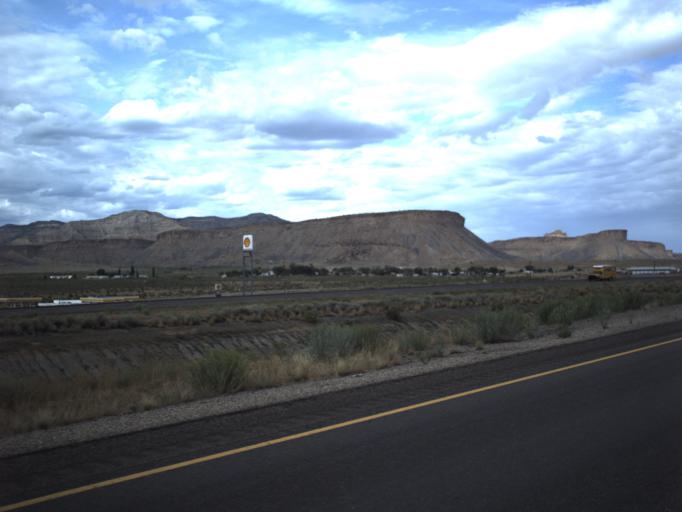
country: US
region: Utah
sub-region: Grand County
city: Moab
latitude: 38.9612
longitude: -109.7245
